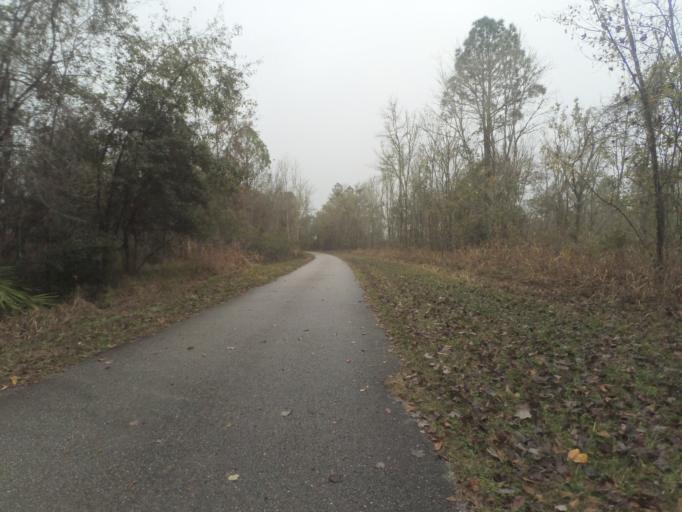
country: US
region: Florida
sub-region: Alachua County
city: Hawthorne
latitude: 29.5902
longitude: -82.1828
